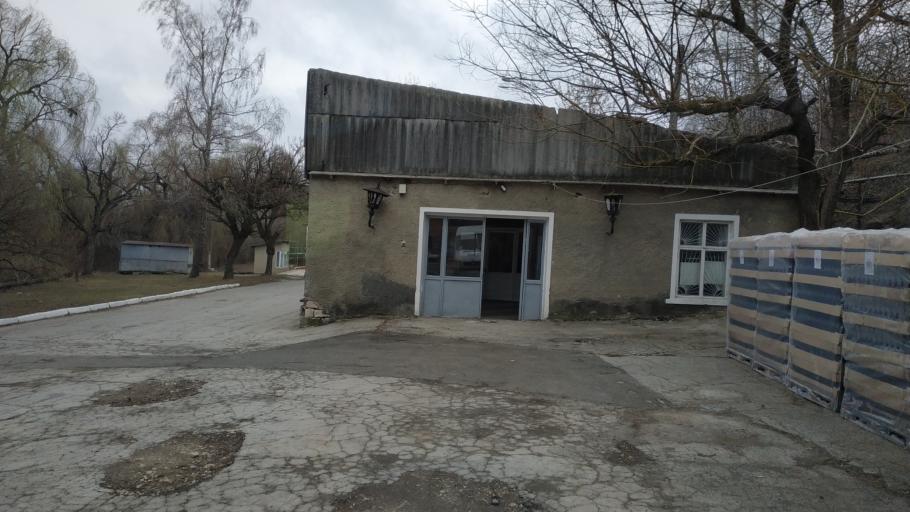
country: MD
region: Laloveni
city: Ialoveni
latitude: 46.9199
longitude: 28.8216
